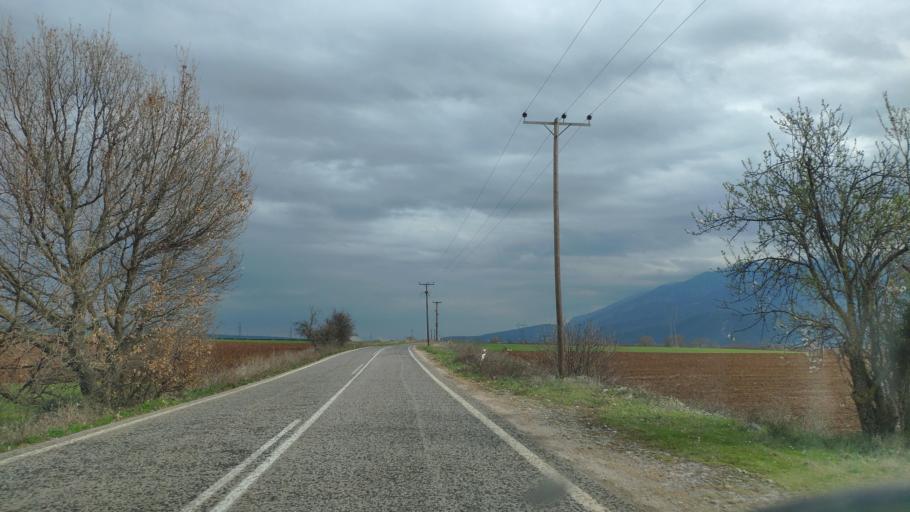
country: GR
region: Central Greece
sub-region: Nomos Fthiotidos
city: Amfikleia
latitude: 38.6993
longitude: 22.5170
